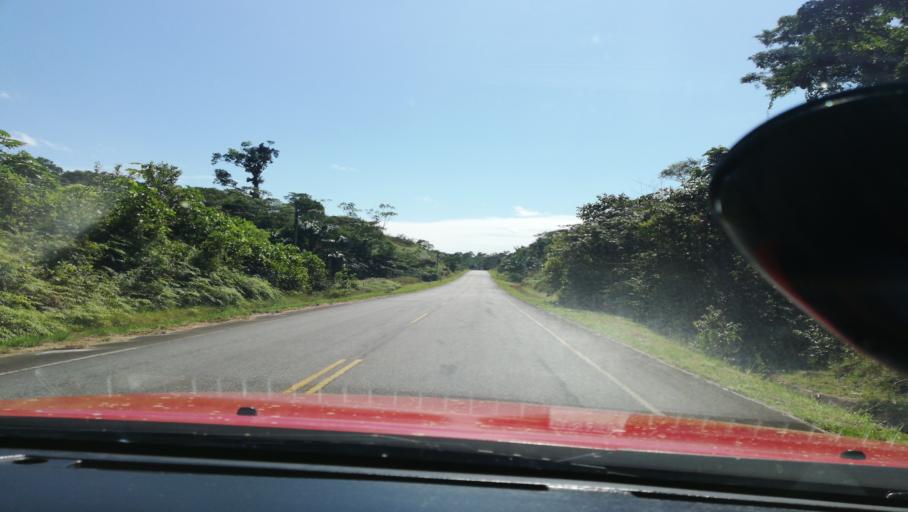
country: PE
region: Loreto
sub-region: Provincia de Loreto
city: Nauta
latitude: -4.3885
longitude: -73.5687
